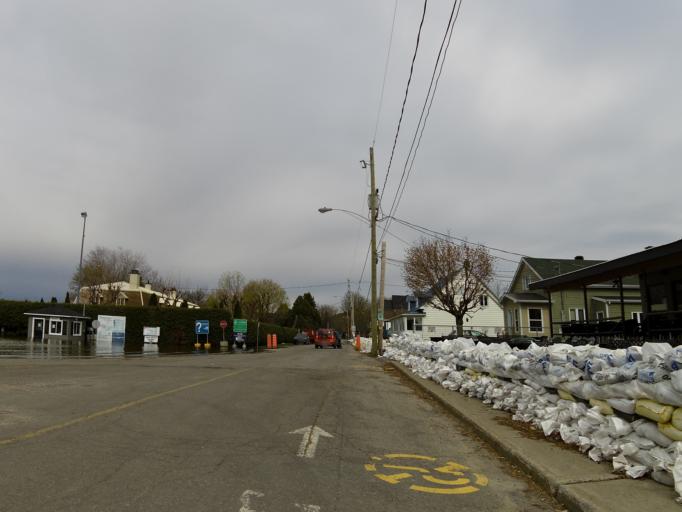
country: CA
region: Quebec
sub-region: Laurentides
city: Oka
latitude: 45.4595
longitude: -74.0907
